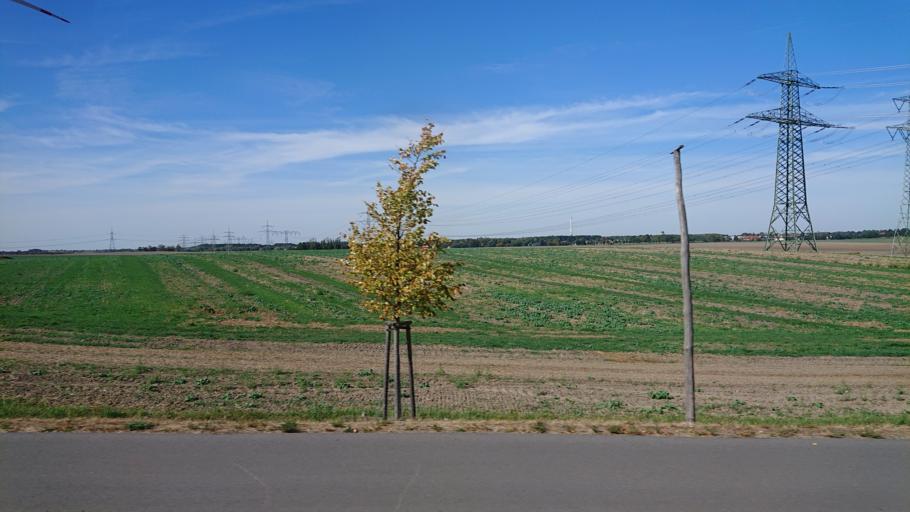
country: DE
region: Berlin
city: Buch
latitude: 52.6177
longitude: 13.5401
